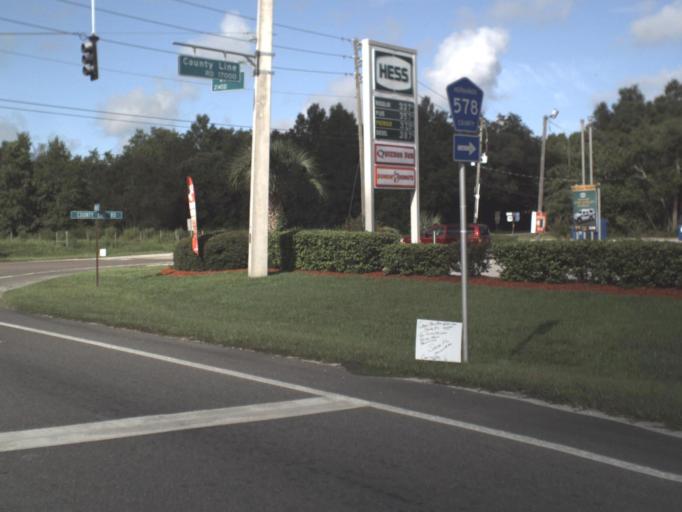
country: US
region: Florida
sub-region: Hernando County
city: Masaryktown
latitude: 28.4340
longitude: -82.4618
